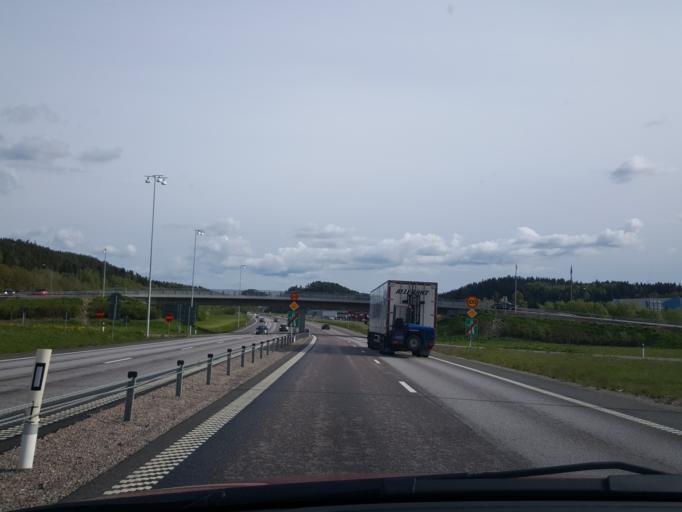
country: SE
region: Vaestra Goetaland
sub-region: Lilla Edets Kommun
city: Lilla Edet
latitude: 58.1257
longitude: 12.1370
